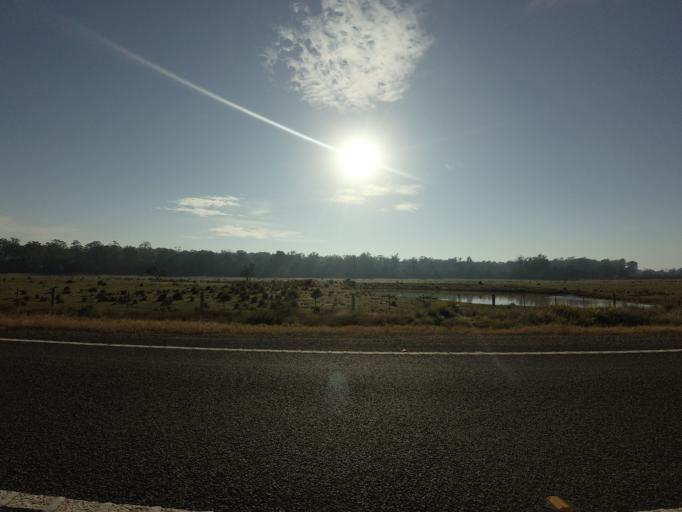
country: AU
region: Tasmania
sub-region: Northern Midlands
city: Longford
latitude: -41.5328
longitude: 147.0416
